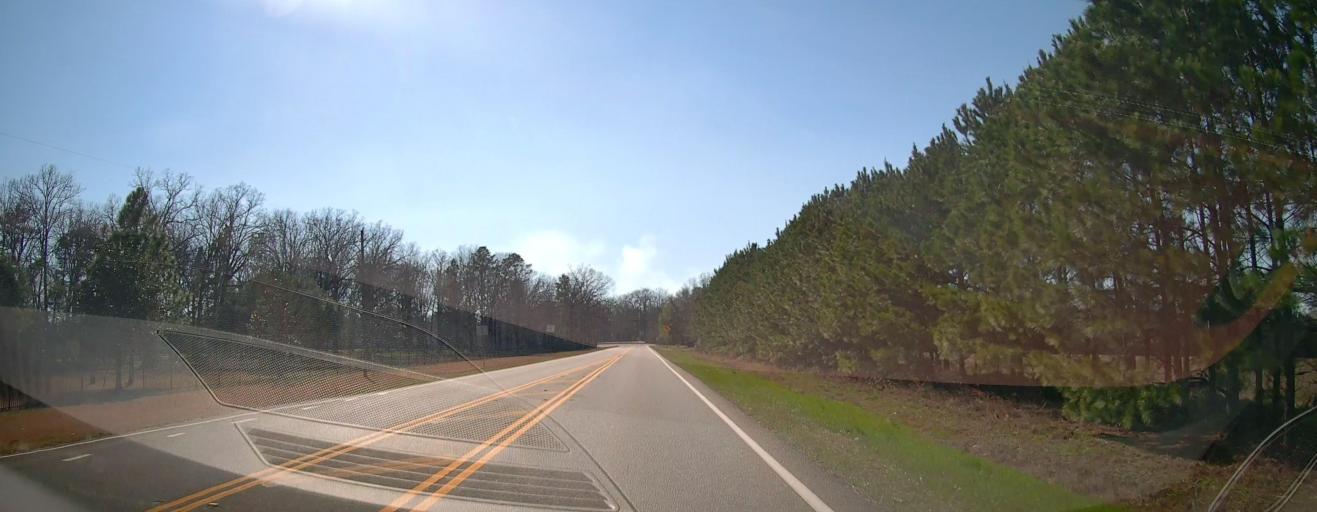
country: US
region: Georgia
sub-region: Macon County
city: Oglethorpe
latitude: 32.2069
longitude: -84.1298
